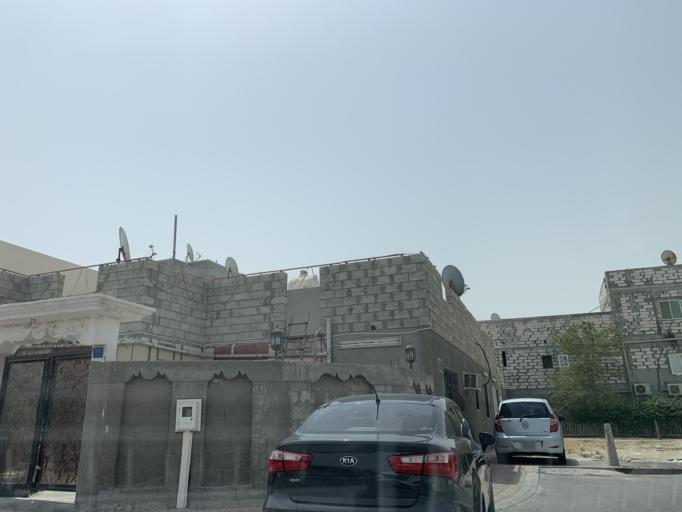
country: BH
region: Northern
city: Madinat `Isa
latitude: 26.1636
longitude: 50.5625
